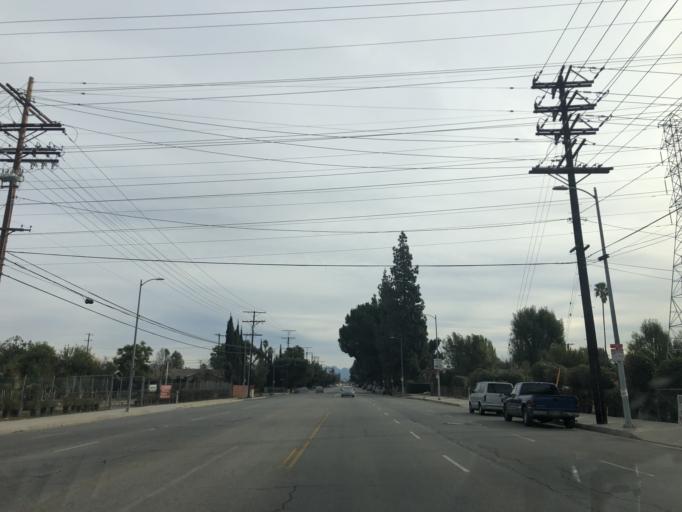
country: US
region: California
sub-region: Los Angeles County
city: Northridge
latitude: 34.2353
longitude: -118.5441
